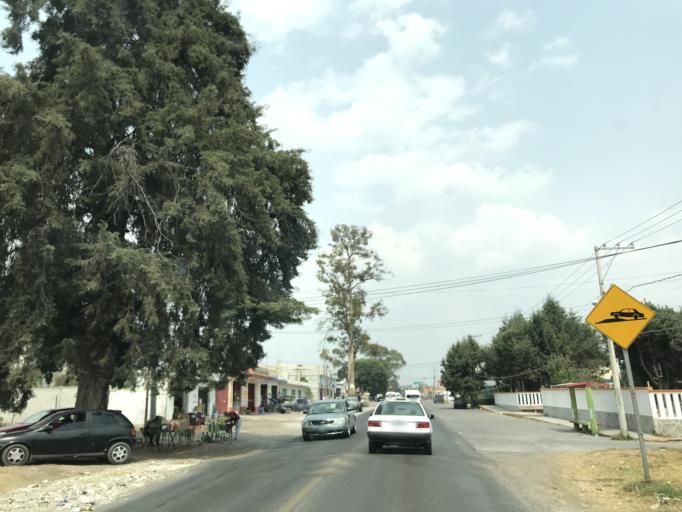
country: MX
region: Tlaxcala
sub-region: Panotla
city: Fraccionamiento la Virgen
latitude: 19.3194
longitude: -98.2749
